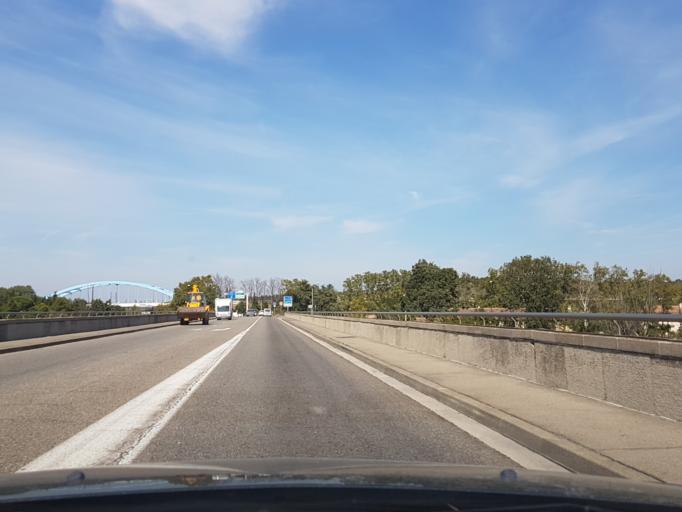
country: FR
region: Provence-Alpes-Cote d'Azur
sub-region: Departement des Bouches-du-Rhone
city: Noves
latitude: 43.8876
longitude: 4.9165
